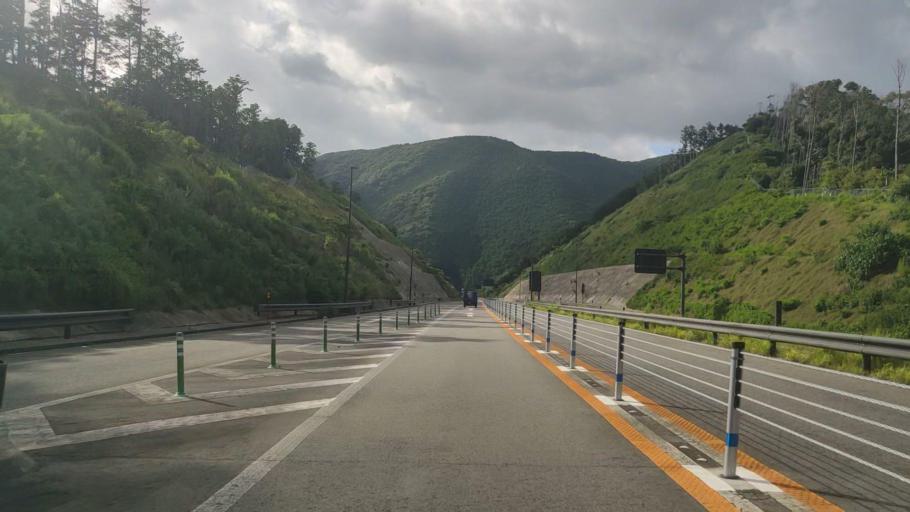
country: JP
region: Wakayama
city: Tanabe
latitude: 33.5570
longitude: 135.5085
